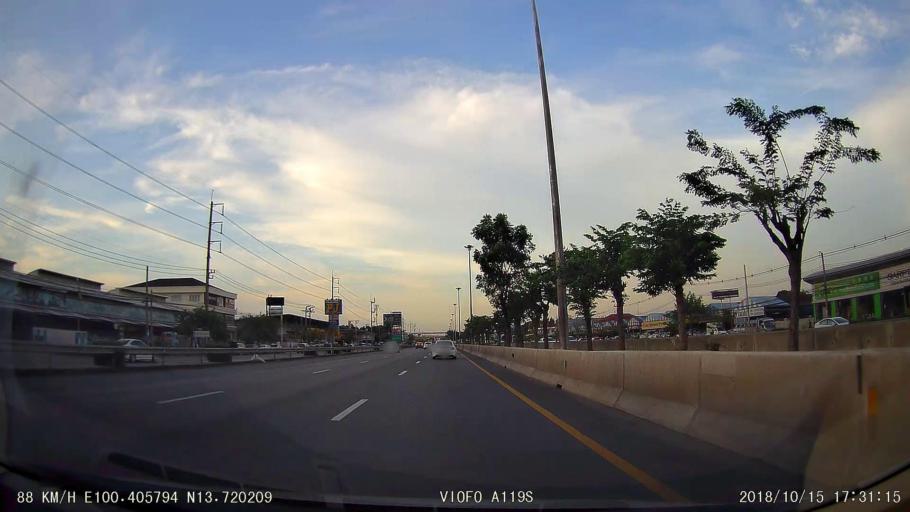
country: TH
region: Bangkok
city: Bang Khae
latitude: 13.7205
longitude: 100.4058
